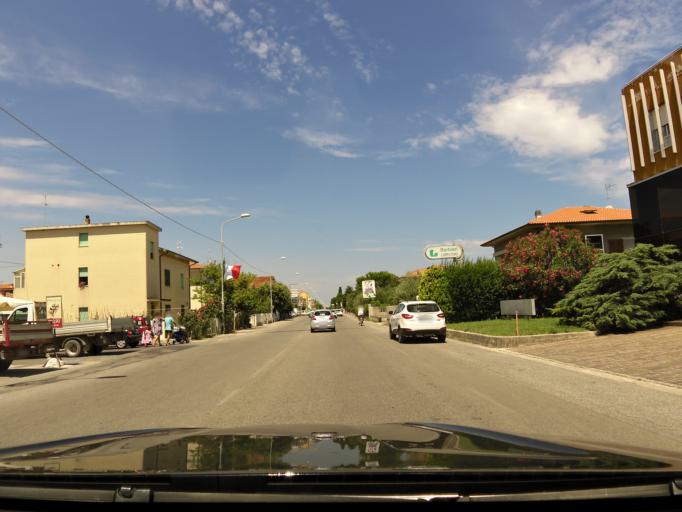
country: IT
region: The Marches
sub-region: Provincia di Ancona
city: Senigallia
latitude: 43.7305
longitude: 13.1973
